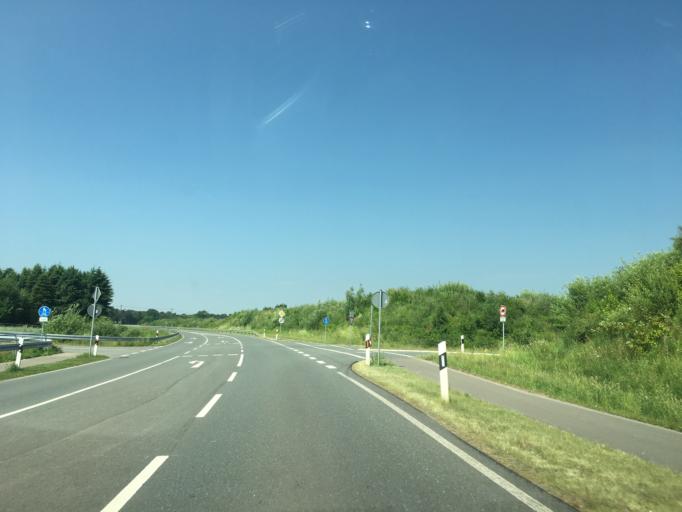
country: DE
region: North Rhine-Westphalia
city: Olfen
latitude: 51.7037
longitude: 7.3634
